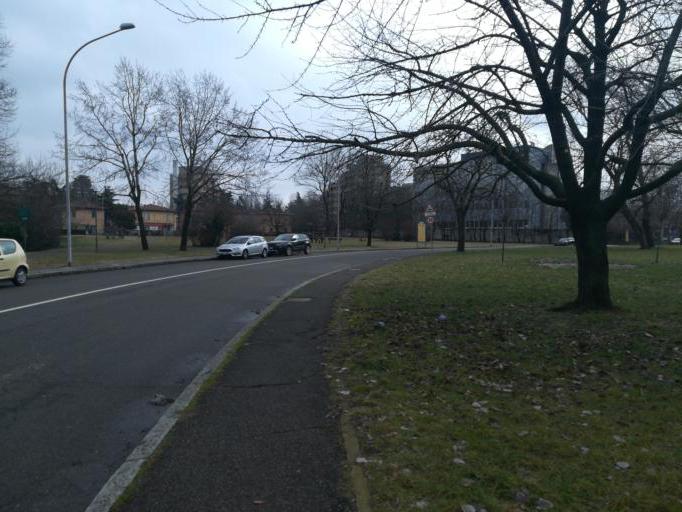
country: IT
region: Emilia-Romagna
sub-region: Provincia di Bologna
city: Progresso
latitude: 44.5411
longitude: 11.3545
